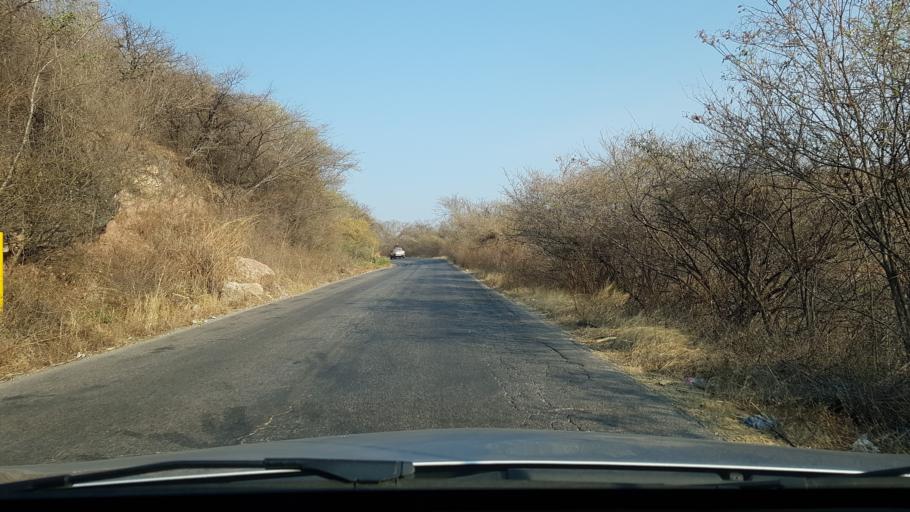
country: MX
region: Morelos
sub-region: Tepalcingo
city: Zacapalco
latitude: 18.6566
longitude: -99.0398
